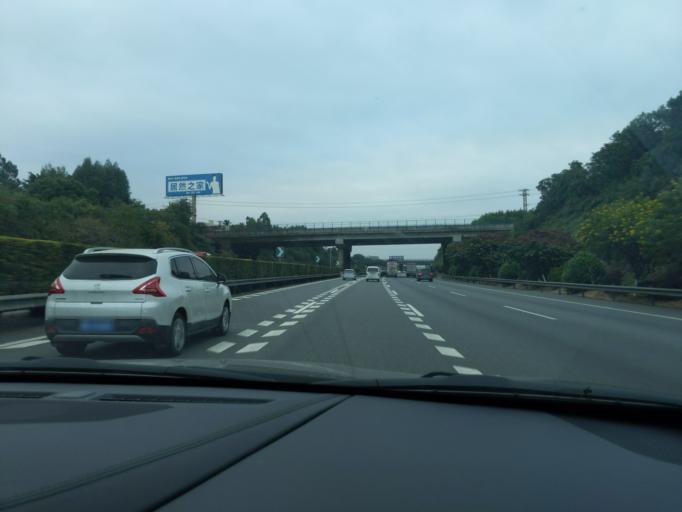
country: CN
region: Fujian
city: Neikeng
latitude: 24.7731
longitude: 118.4555
